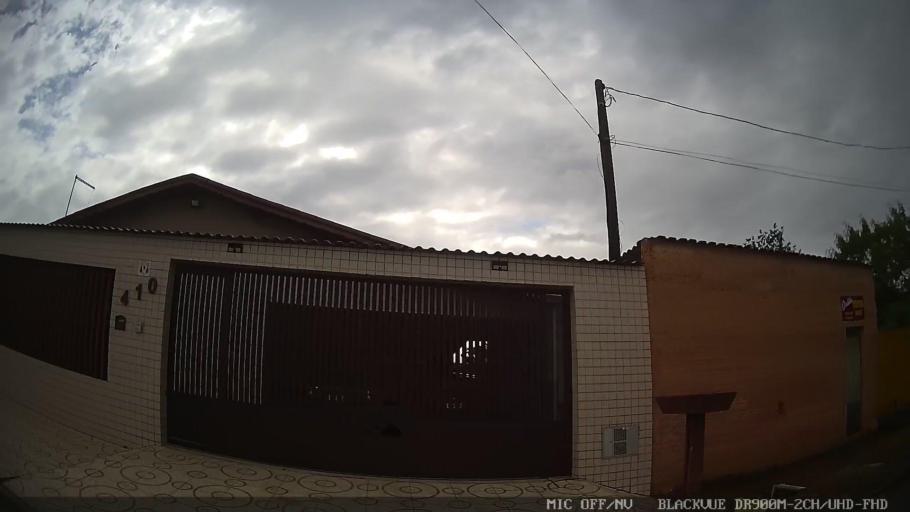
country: BR
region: Sao Paulo
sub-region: Itanhaem
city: Itanhaem
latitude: -24.1901
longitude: -46.8122
